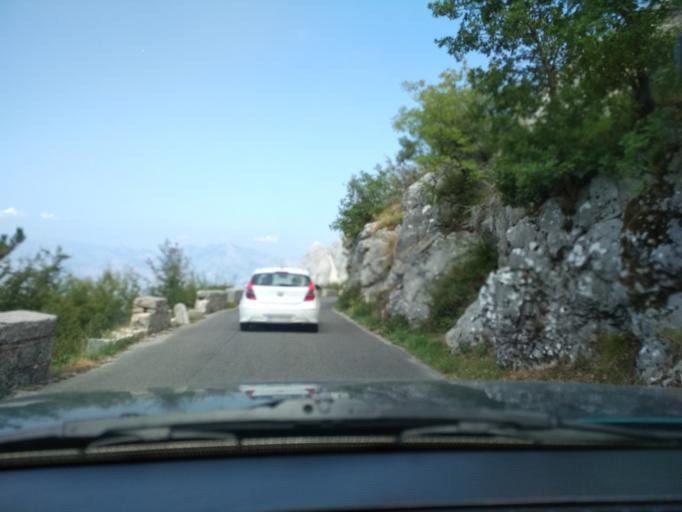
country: ME
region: Kotor
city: Kotor
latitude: 42.4111
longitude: 18.7902
